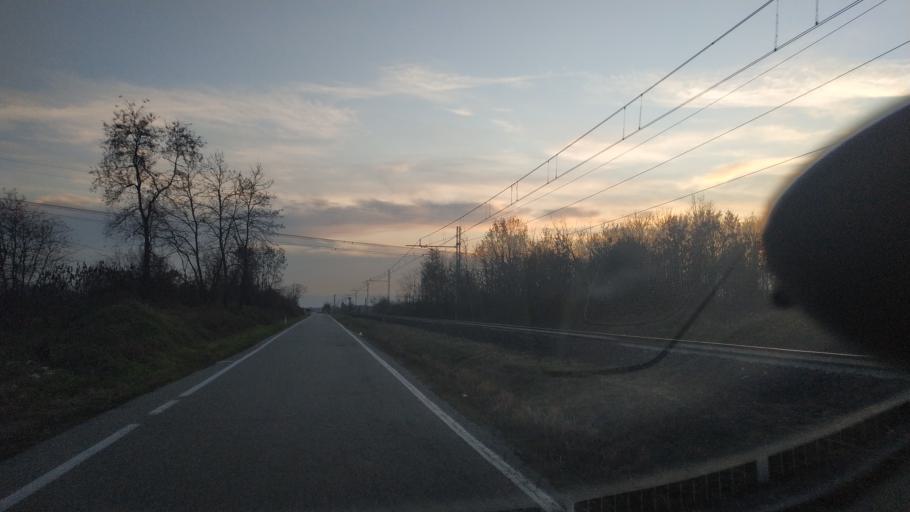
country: IT
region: Piedmont
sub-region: Provincia di Torino
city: Montanaro
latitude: 45.2622
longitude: 7.8695
